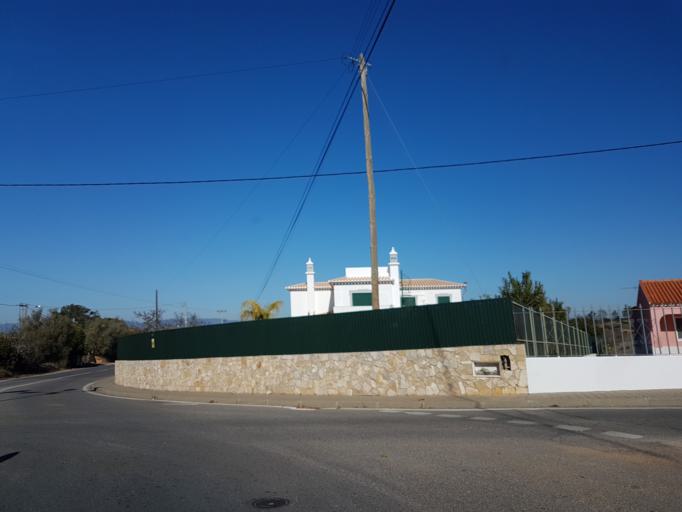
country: PT
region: Faro
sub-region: Lagoa
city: Carvoeiro
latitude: 37.1016
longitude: -8.4438
